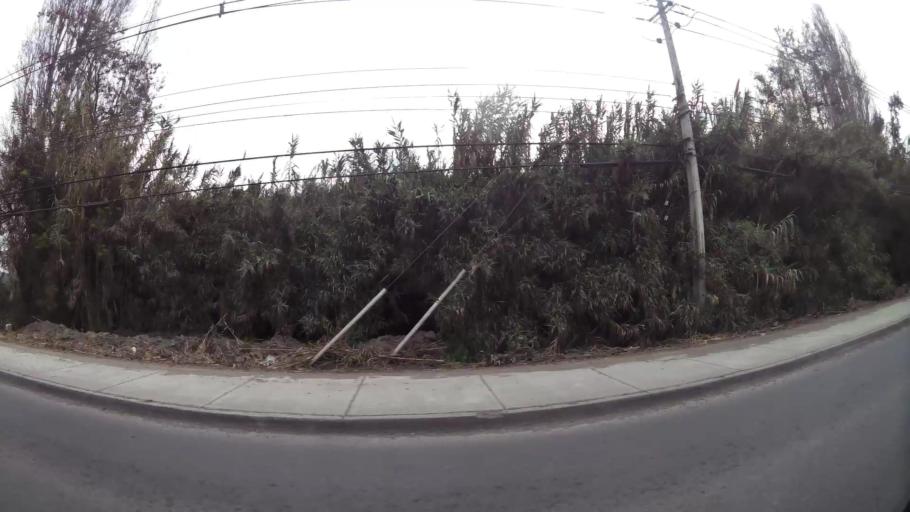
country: CL
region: Santiago Metropolitan
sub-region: Provincia de Chacabuco
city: Chicureo Abajo
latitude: -33.2810
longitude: -70.7032
